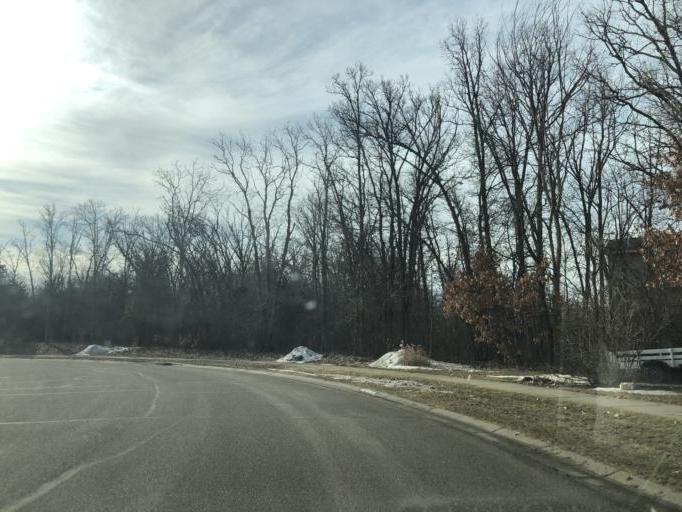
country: US
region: Minnesota
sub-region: Sherburne County
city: Becker
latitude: 45.4012
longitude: -93.8524
